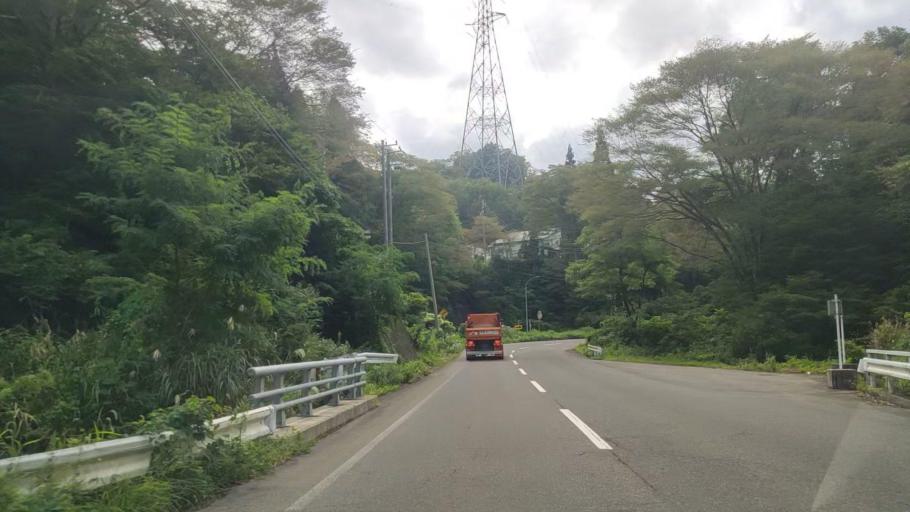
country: JP
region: Nagano
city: Iiyama
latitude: 36.8910
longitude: 138.3236
